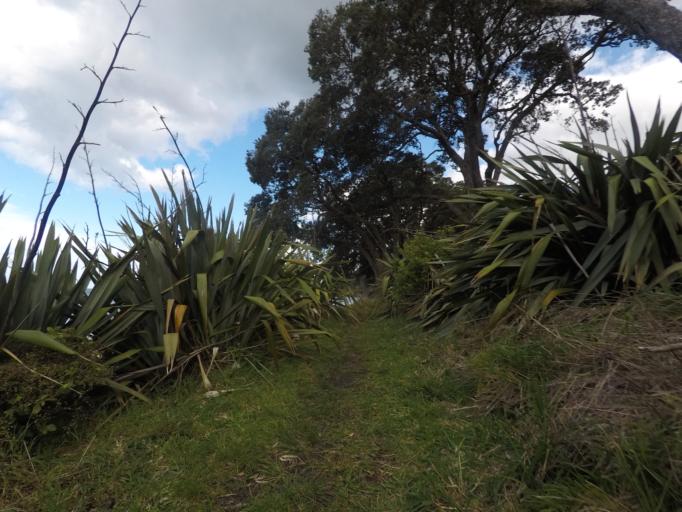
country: NZ
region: Bay of Plenty
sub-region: Western Bay of Plenty District
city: Waihi Beach
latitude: -37.3831
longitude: 175.9376
